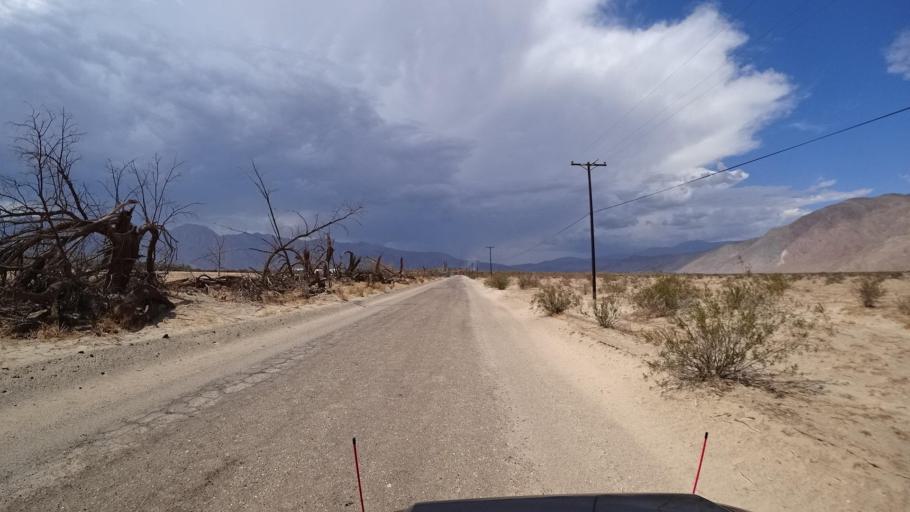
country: US
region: California
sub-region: San Diego County
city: Borrego Springs
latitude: 33.2974
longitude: -116.3352
